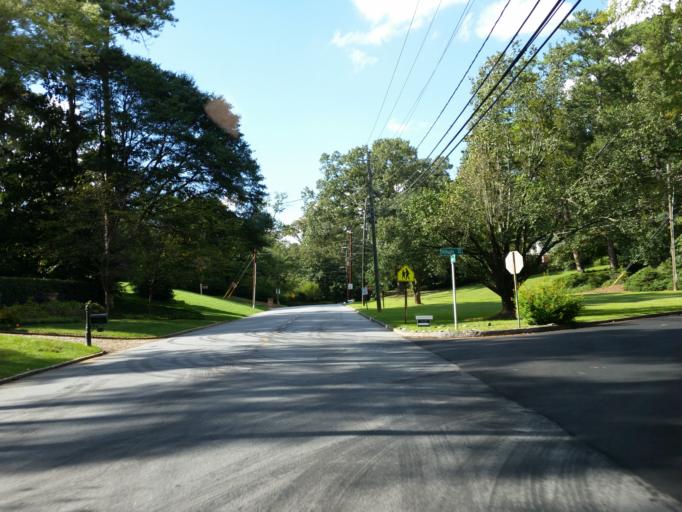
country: US
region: Georgia
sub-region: Cobb County
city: Vinings
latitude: 33.8672
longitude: -84.4063
